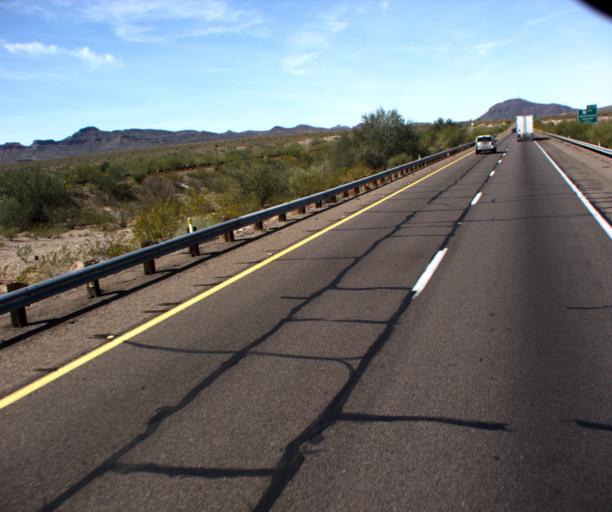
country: US
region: Arizona
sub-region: La Paz County
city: Quartzsite
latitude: 33.6591
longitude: -113.9868
